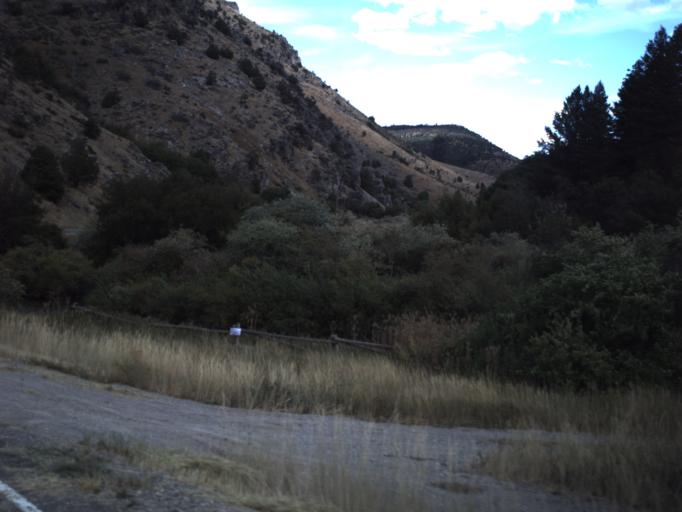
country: US
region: Utah
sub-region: Cache County
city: Millville
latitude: 41.6205
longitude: -111.6584
